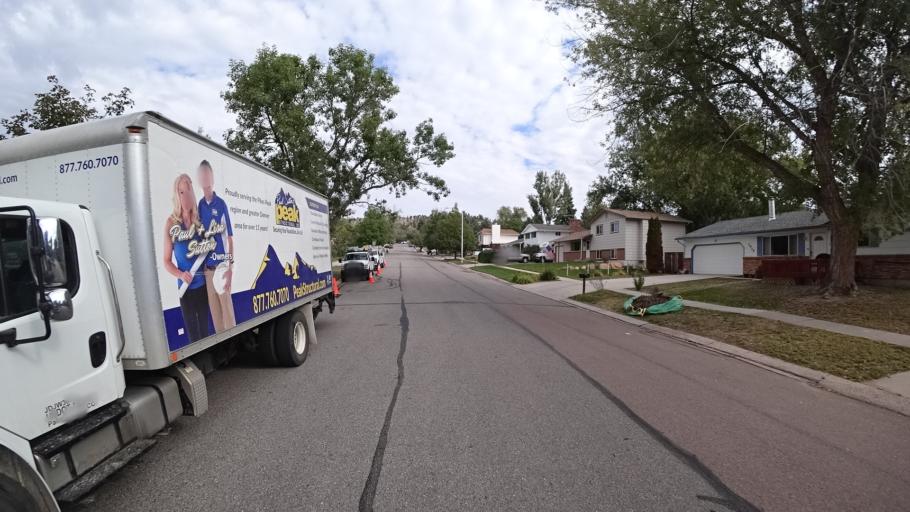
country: US
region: Colorado
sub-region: El Paso County
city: Cimarron Hills
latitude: 38.8534
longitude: -104.7412
